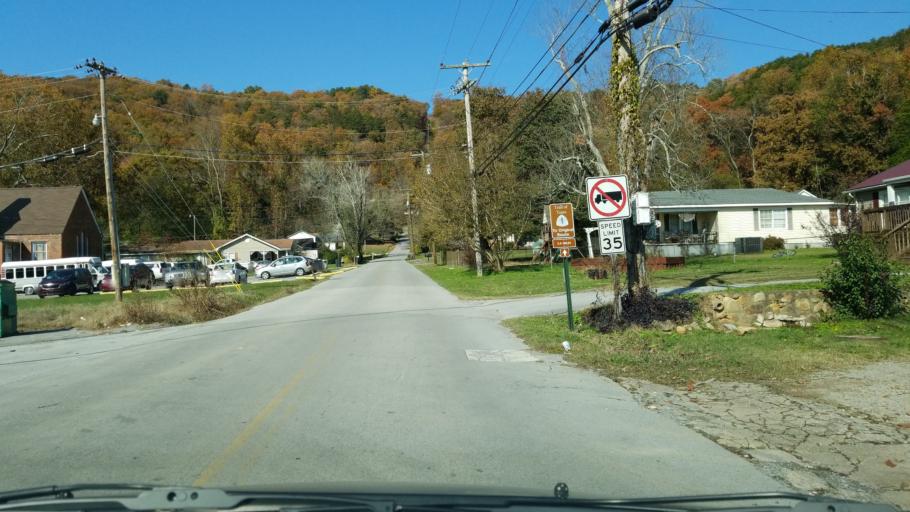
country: US
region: Tennessee
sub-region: Hamilton County
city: Soddy-Daisy
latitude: 35.2429
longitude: -85.1925
